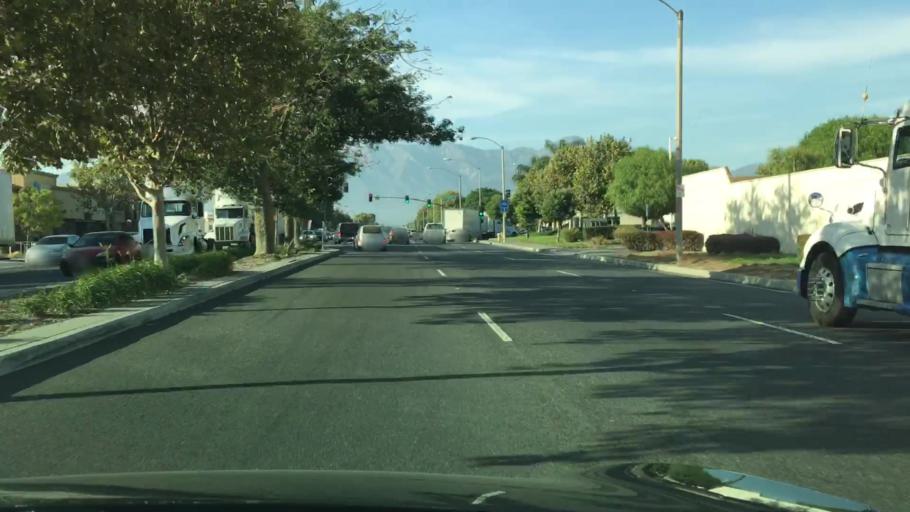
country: US
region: California
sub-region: San Bernardino County
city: Ontario
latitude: 34.0328
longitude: -117.6284
